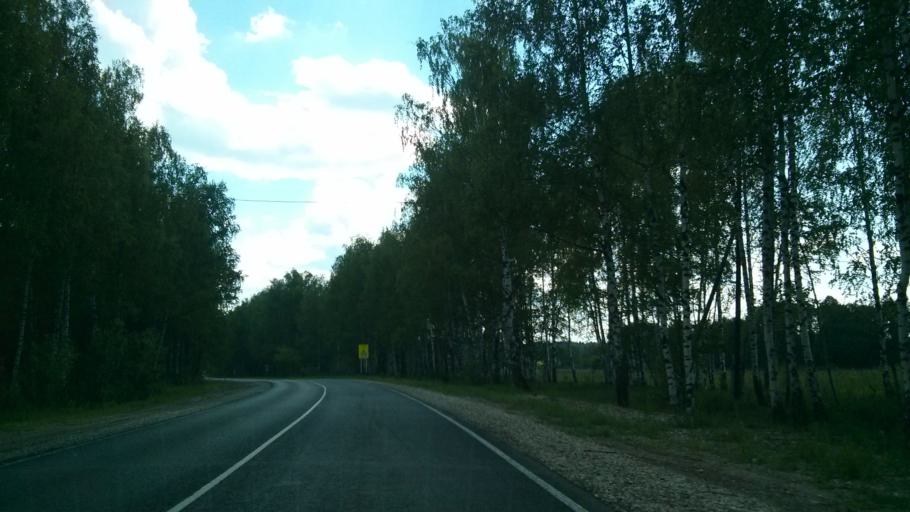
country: RU
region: Vladimir
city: Murom
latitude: 55.5152
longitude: 41.9283
